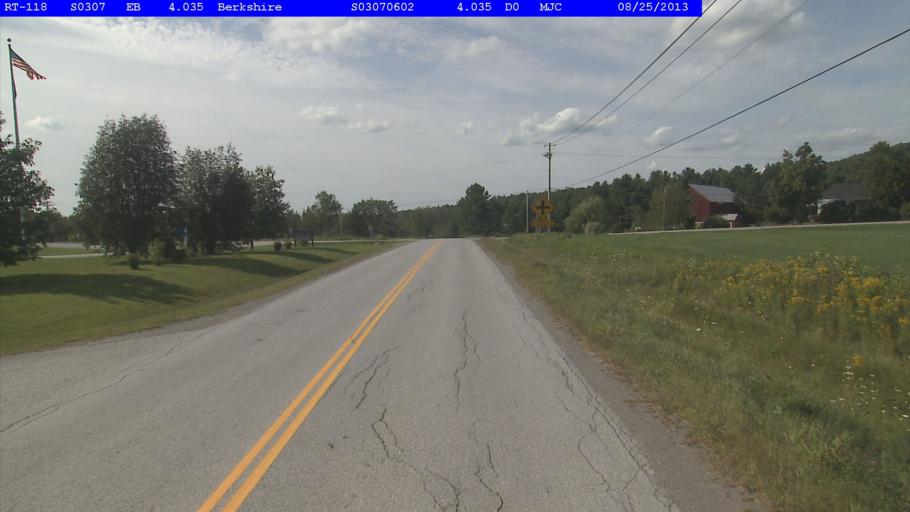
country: US
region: Vermont
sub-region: Franklin County
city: Enosburg Falls
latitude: 44.9725
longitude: -72.7653
